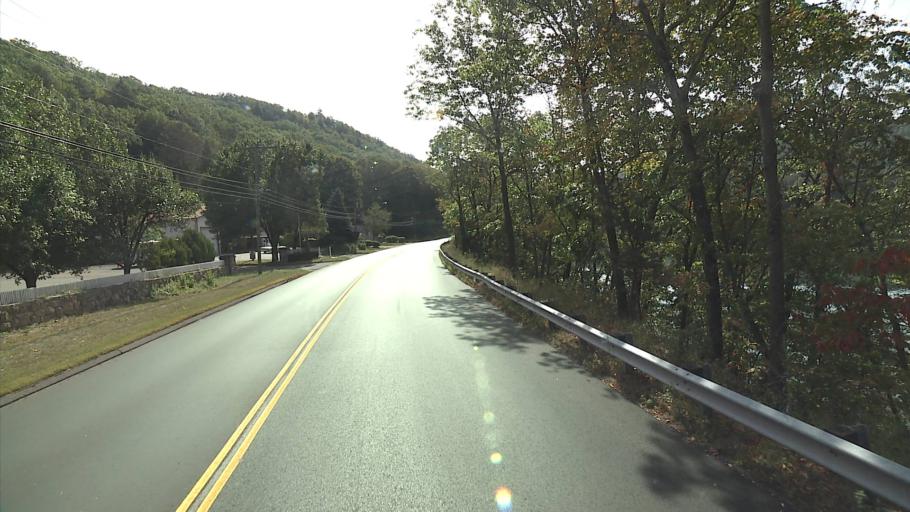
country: US
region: Connecticut
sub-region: New Haven County
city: Ansonia
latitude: 41.3624
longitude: -73.1384
